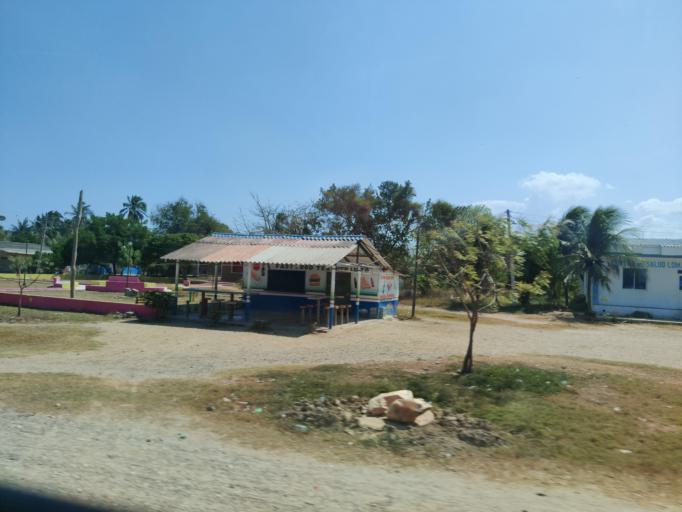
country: CO
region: Bolivar
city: Santa Catalina
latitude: 10.7380
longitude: -75.2635
